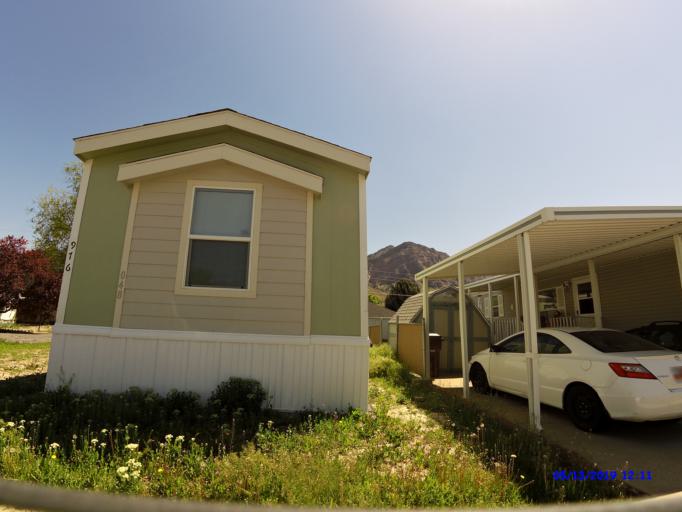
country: US
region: Utah
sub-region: Weber County
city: Harrisville
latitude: 41.2753
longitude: -111.9649
